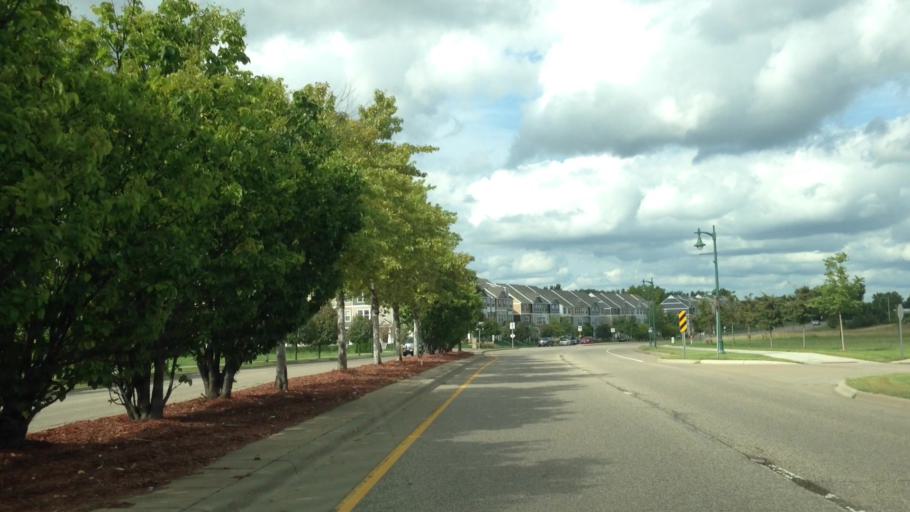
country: US
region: Minnesota
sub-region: Ramsey County
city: New Brighton
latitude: 45.0692
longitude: -93.1928
